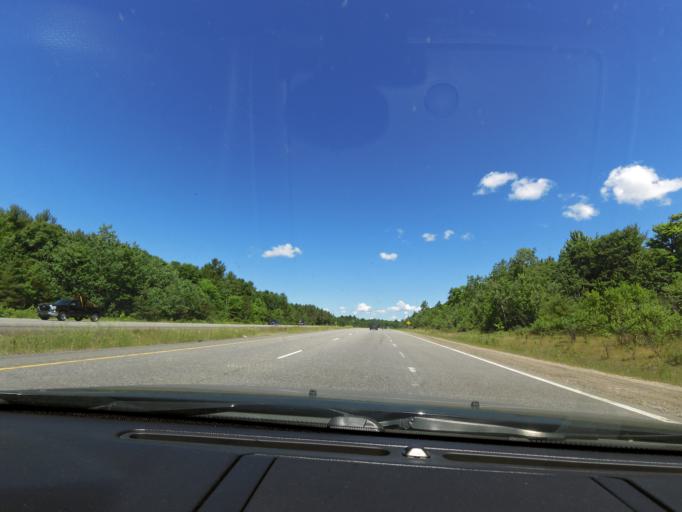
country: CA
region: Ontario
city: Bracebridge
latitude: 45.0575
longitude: -79.2931
